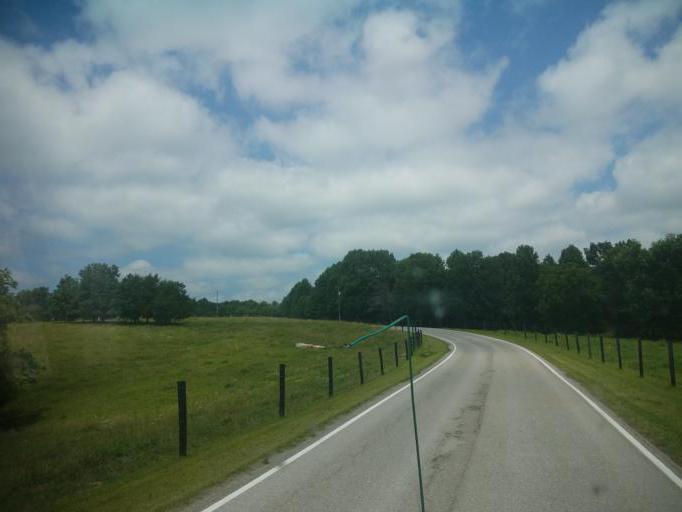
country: US
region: Kentucky
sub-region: Hart County
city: Munfordville
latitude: 37.3489
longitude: -86.0365
